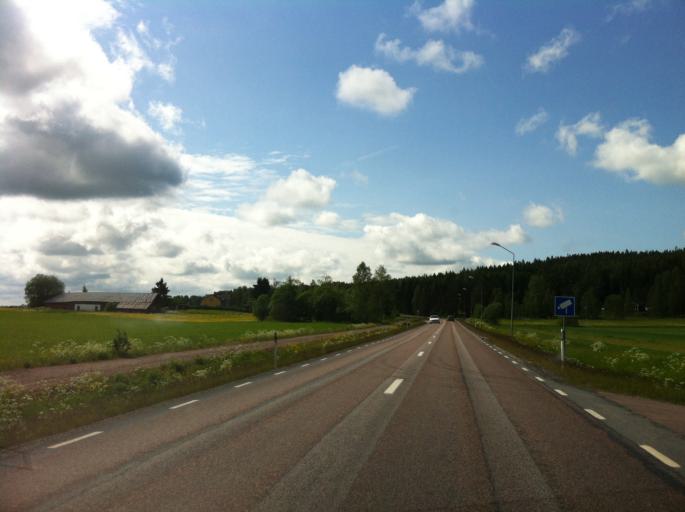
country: SE
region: Vaermland
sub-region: Karlstads Kommun
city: Edsvalla
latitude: 59.6190
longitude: 13.1569
